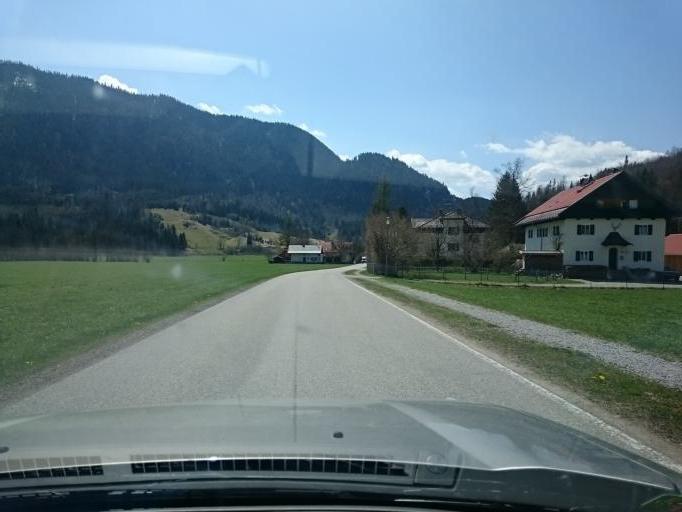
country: DE
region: Bavaria
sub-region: Upper Bavaria
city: Jachenau
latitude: 47.6038
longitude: 11.4321
